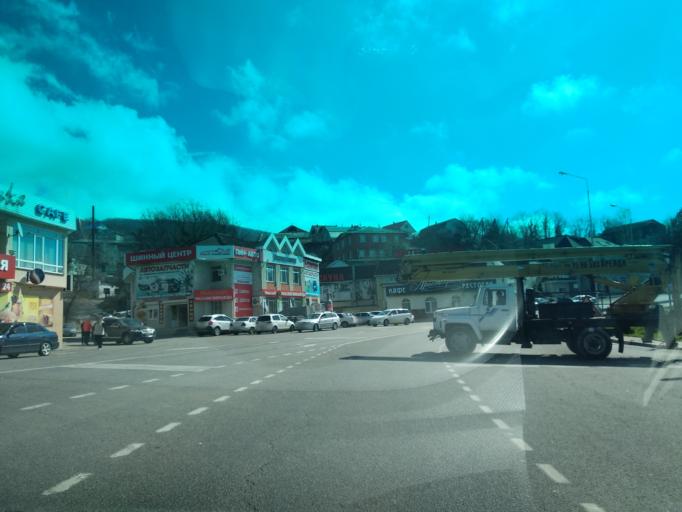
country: RU
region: Krasnodarskiy
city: Tuapse
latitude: 44.0928
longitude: 39.1169
